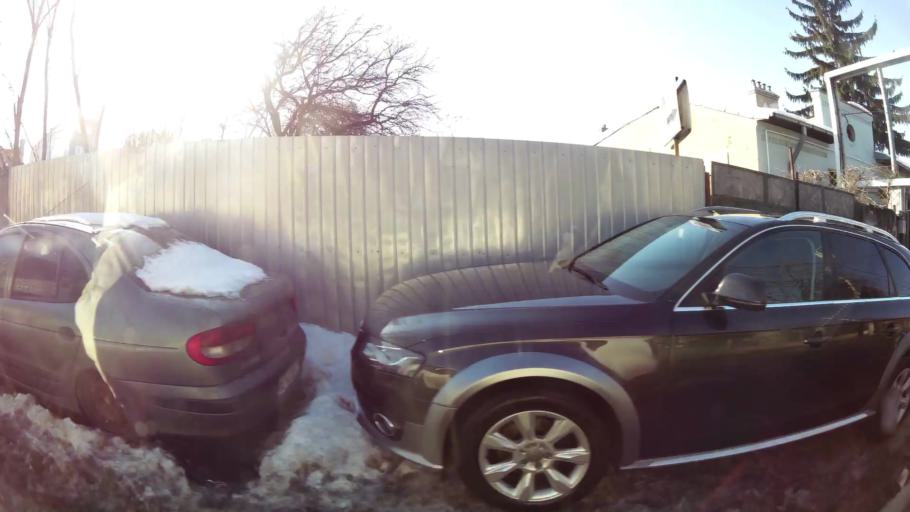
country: RO
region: Bucuresti
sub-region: Municipiul Bucuresti
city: Bucharest
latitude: 44.4662
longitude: 26.1152
